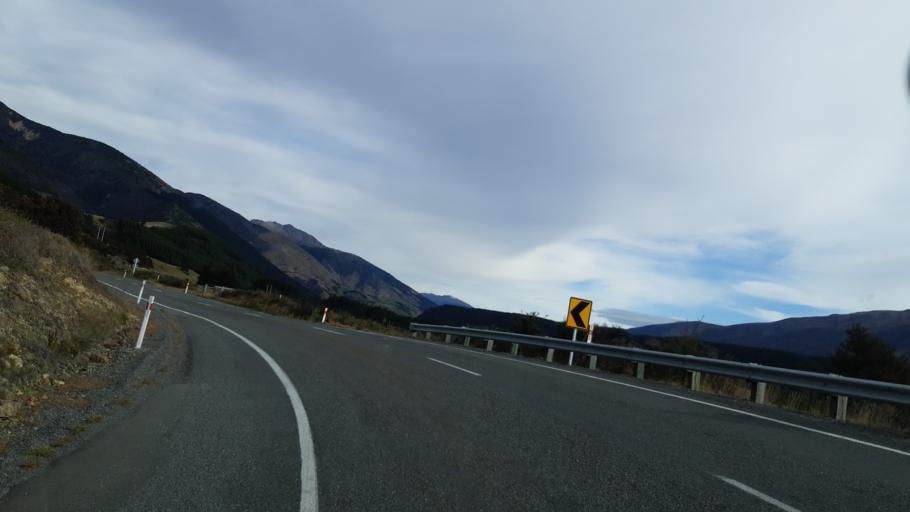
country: NZ
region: Tasman
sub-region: Tasman District
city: Wakefield
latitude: -41.6962
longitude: 173.1337
